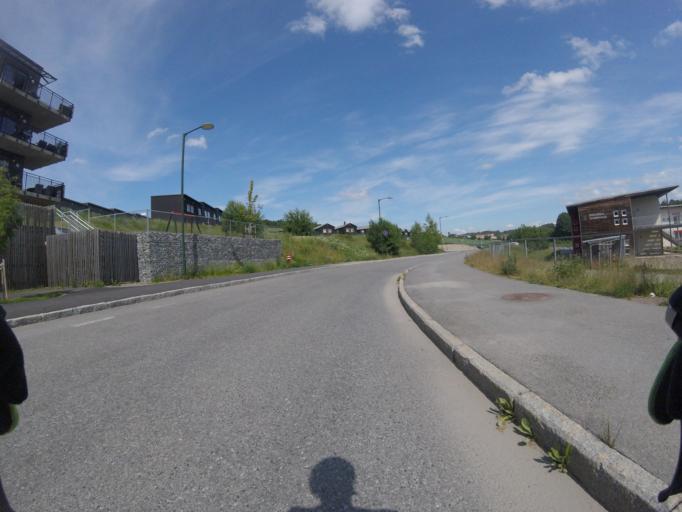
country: NO
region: Akershus
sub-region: Skedsmo
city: Lillestrom
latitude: 59.9772
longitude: 11.0406
